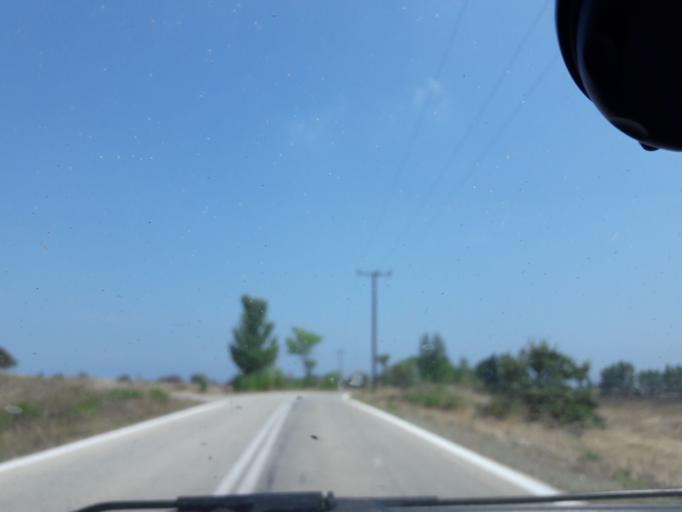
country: GR
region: North Aegean
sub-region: Nomos Lesvou
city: Myrina
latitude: 39.9245
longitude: 25.3269
